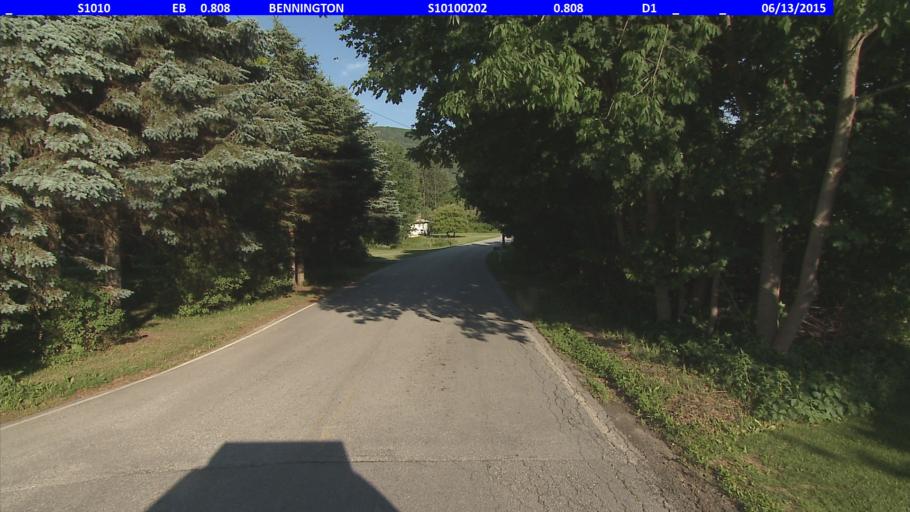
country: US
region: Vermont
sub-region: Bennington County
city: Bennington
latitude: 42.8768
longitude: -73.1603
